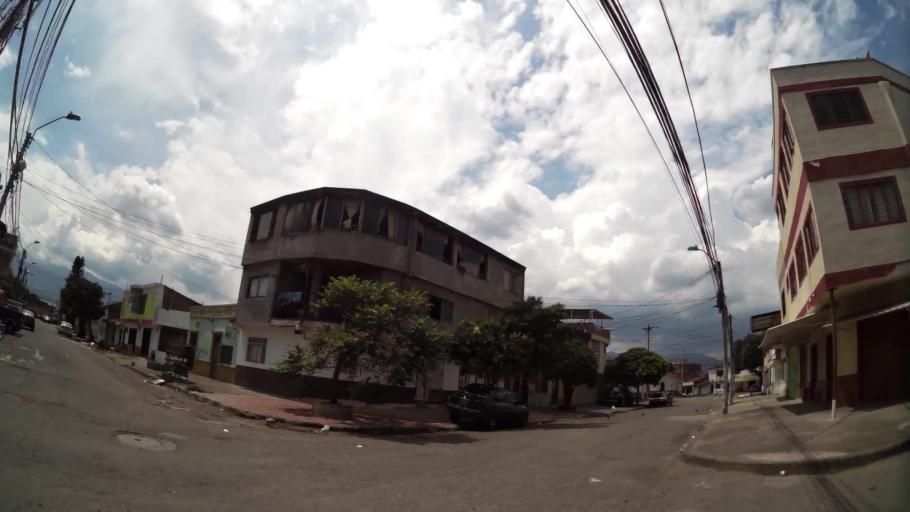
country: CO
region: Valle del Cauca
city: Cali
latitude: 3.4417
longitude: -76.5143
